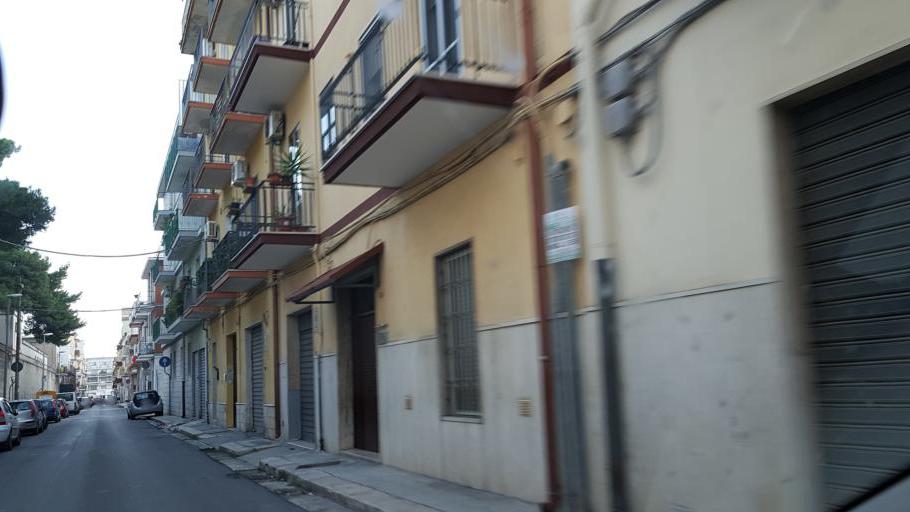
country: IT
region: Apulia
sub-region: Provincia di Brindisi
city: Brindisi
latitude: 40.6357
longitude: 17.9305
